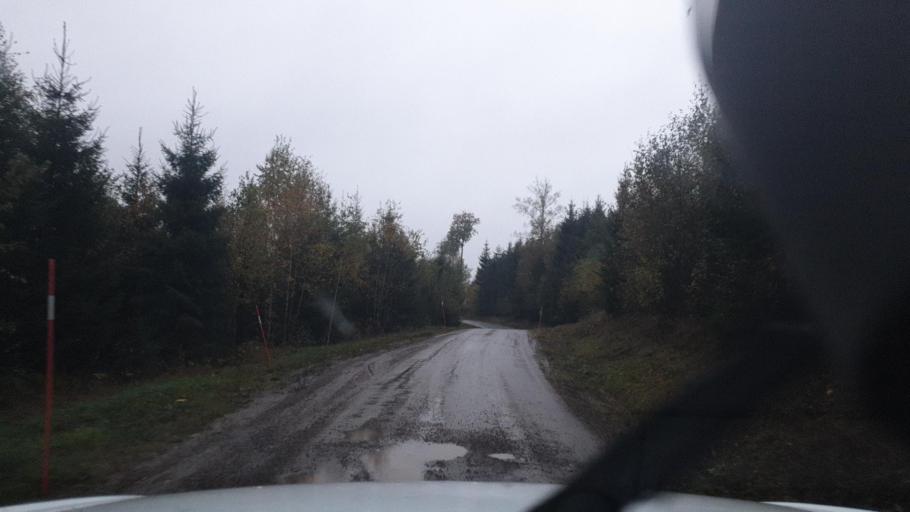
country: SE
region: Vaermland
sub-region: Eda Kommun
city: Amotfors
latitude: 59.7938
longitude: 12.4262
